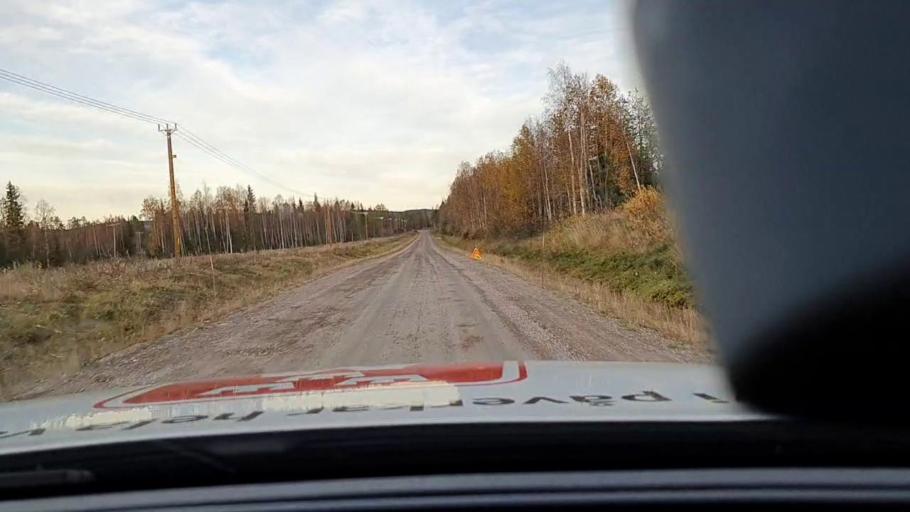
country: SE
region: Norrbotten
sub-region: Overkalix Kommun
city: OEverkalix
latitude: 66.3273
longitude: 22.5493
